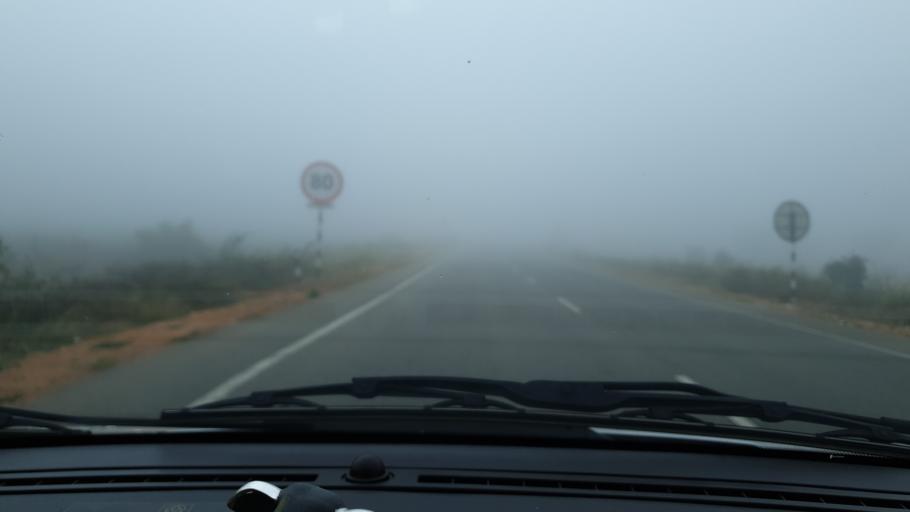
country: IN
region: Telangana
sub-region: Mahbubnagar
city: Nagar Karnul
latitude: 16.6742
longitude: 78.5304
